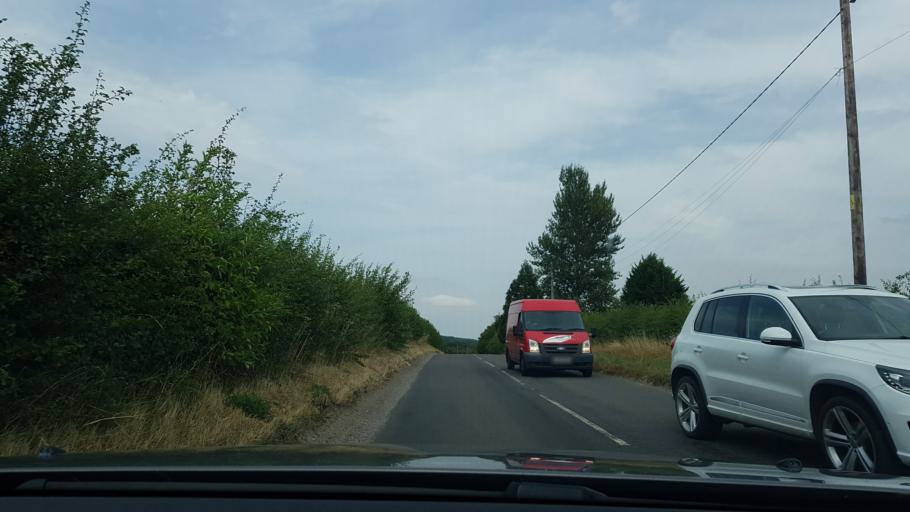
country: GB
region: England
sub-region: Wiltshire
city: Shalbourne
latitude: 51.3796
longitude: -1.5363
